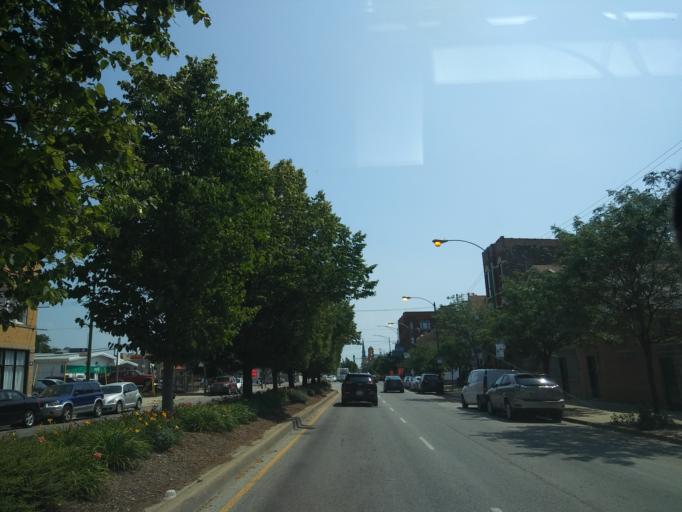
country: US
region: Illinois
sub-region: Cook County
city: Chicago
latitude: 41.8921
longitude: -87.6672
